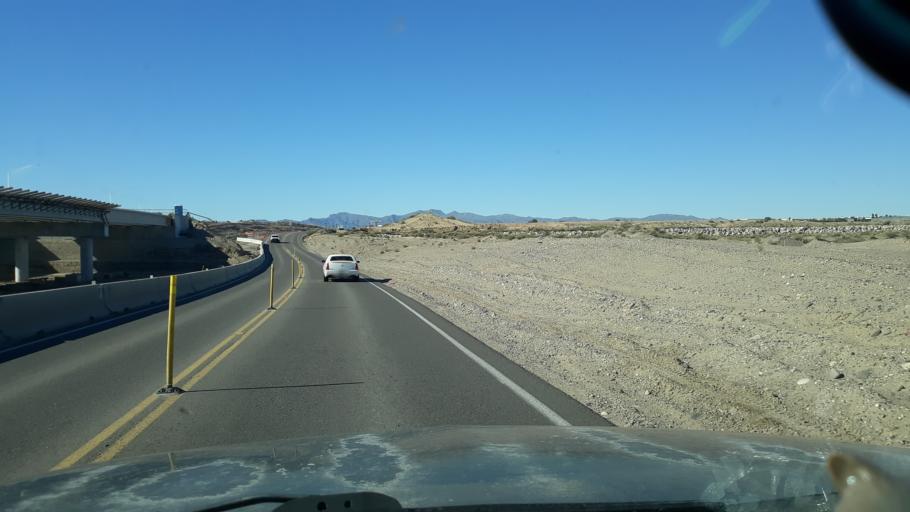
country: US
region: Arizona
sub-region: Maricopa County
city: Youngtown
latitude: 33.5512
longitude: -112.3167
